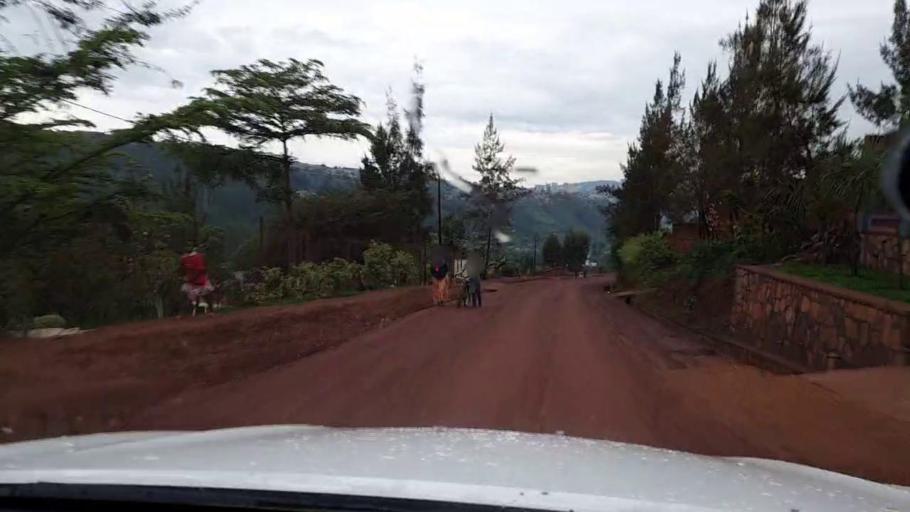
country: RW
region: Kigali
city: Kigali
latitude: -1.9056
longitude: 30.0460
